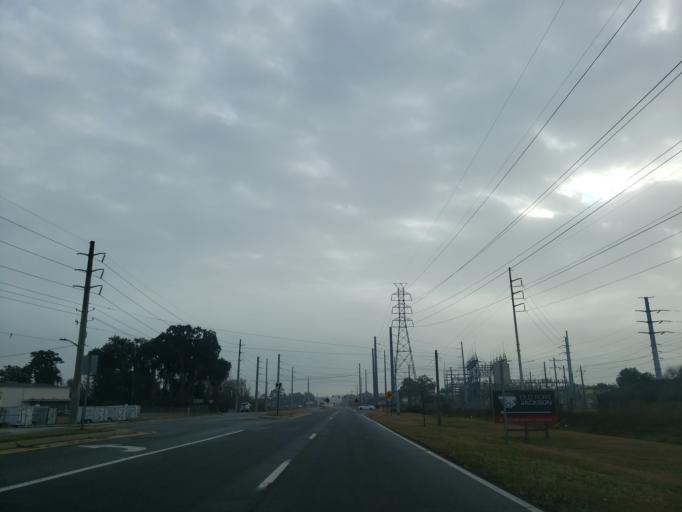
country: US
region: Georgia
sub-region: Chatham County
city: Thunderbolt
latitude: 32.0678
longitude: -81.0504
